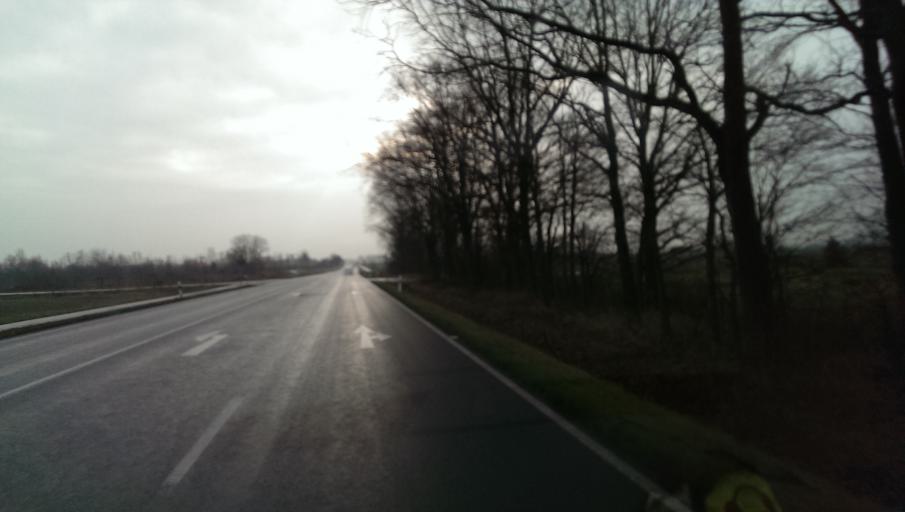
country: DE
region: Saxony
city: Grossenhain
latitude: 51.3186
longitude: 13.5402
